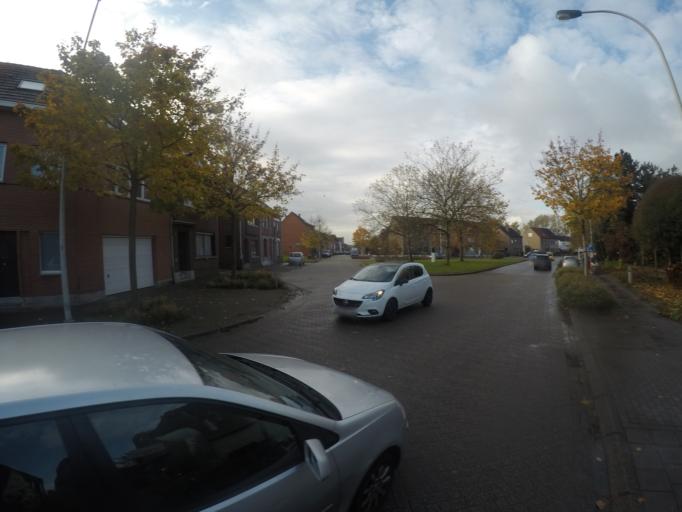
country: BE
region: Flanders
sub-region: Provincie Antwerpen
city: Zwijndrecht
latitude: 51.2066
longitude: 4.3417
